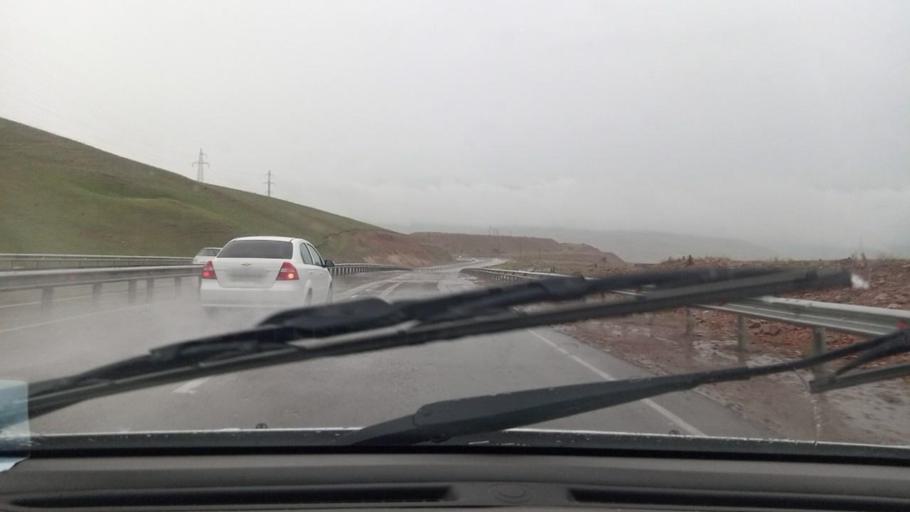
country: UZ
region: Toshkent
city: Angren
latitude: 41.0611
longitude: 70.1827
